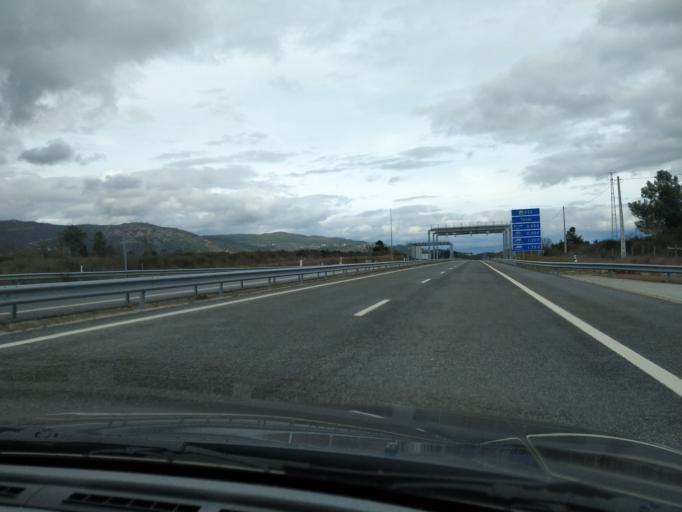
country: PT
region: Vila Real
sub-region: Chaves
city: Chaves
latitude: 41.7502
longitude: -7.5203
